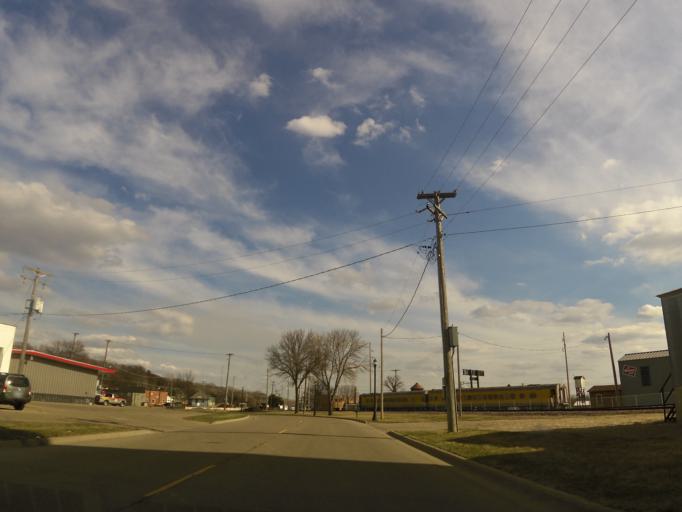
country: US
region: Minnesota
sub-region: Chippewa County
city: Montevideo
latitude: 44.9429
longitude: -95.7255
